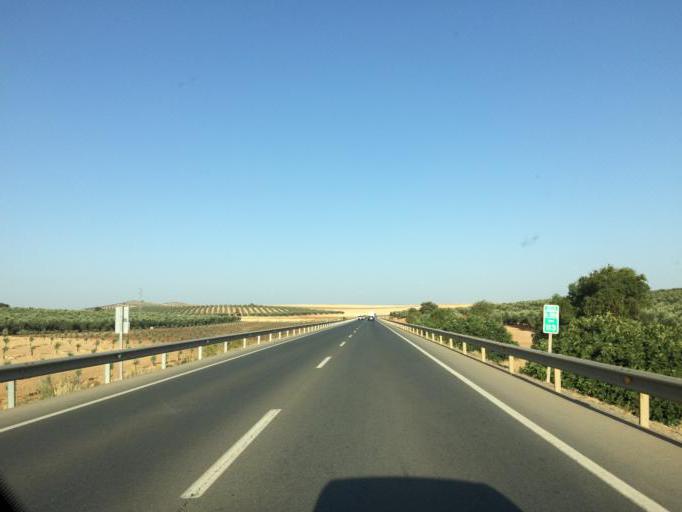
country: ES
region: Andalusia
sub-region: Provincia de Malaga
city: Campillos
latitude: 37.0511
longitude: -4.7943
